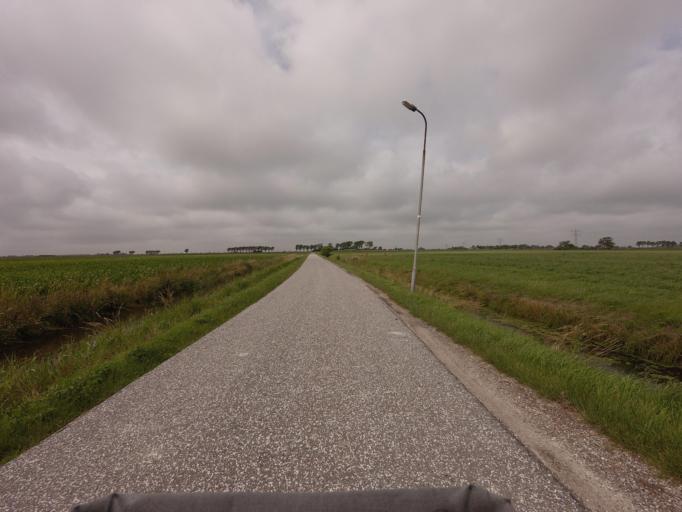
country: NL
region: North Holland
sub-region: Gemeente Schagen
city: Schagen
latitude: 52.7960
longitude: 4.8257
